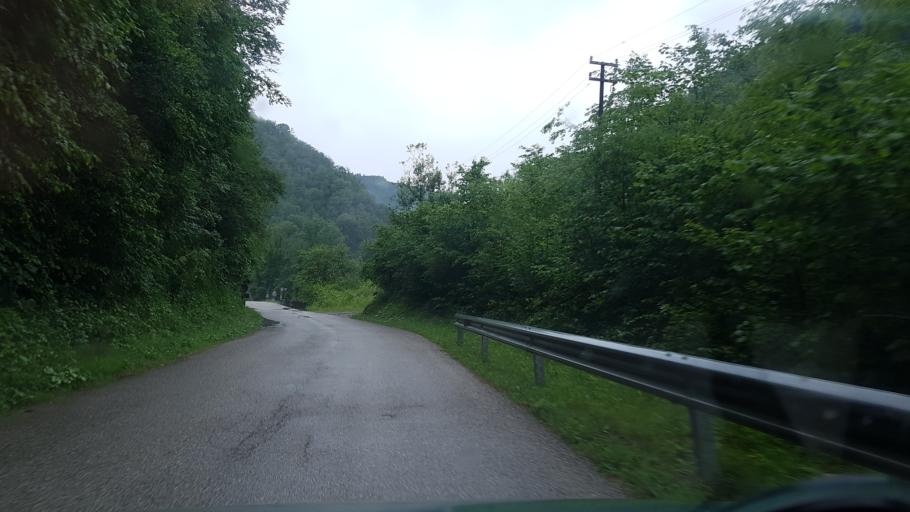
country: IT
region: Friuli Venezia Giulia
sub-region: Provincia di Udine
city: Taipana
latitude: 46.2528
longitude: 13.3194
